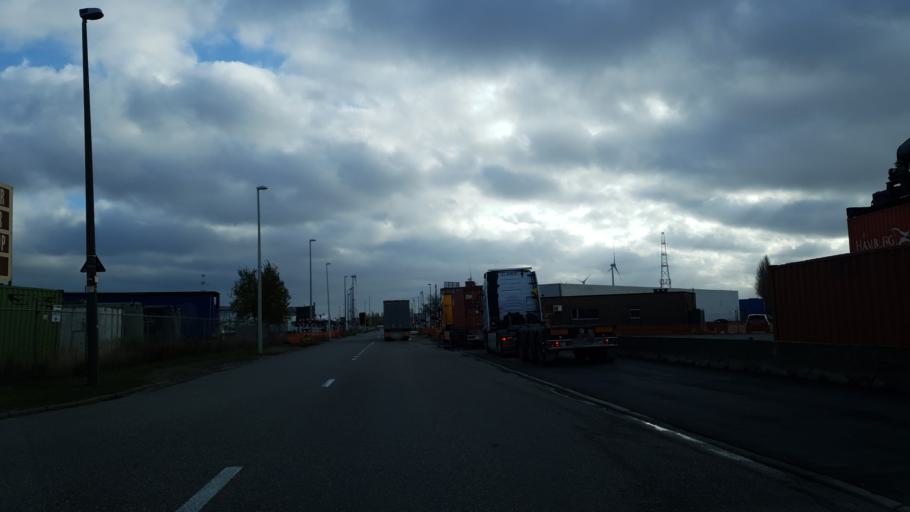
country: BE
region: Flanders
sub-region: Provincie Antwerpen
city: Antwerpen
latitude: 51.2698
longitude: 4.3736
